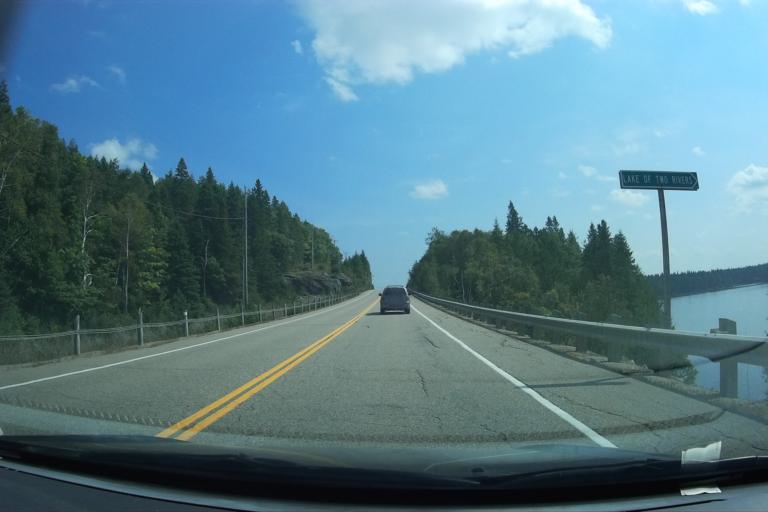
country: CA
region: Ontario
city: Mattawa
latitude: 45.5823
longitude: -78.4662
